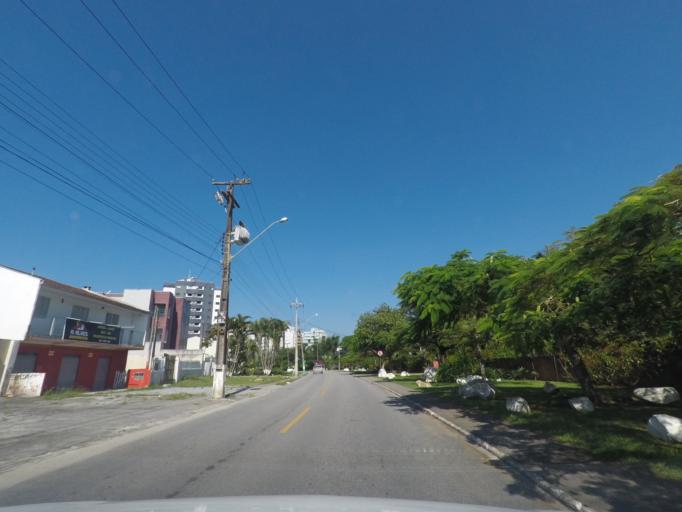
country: BR
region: Parana
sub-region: Guaratuba
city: Guaratuba
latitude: -25.8330
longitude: -48.5397
